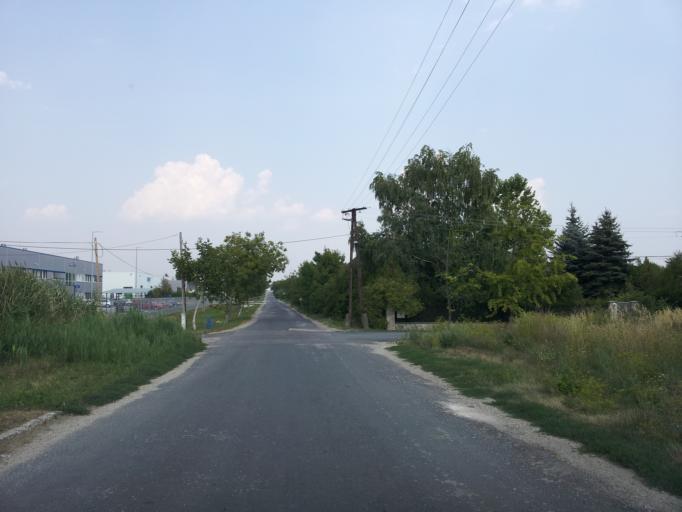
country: HU
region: Gyor-Moson-Sopron
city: Nyul
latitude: 47.5883
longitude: 17.6979
